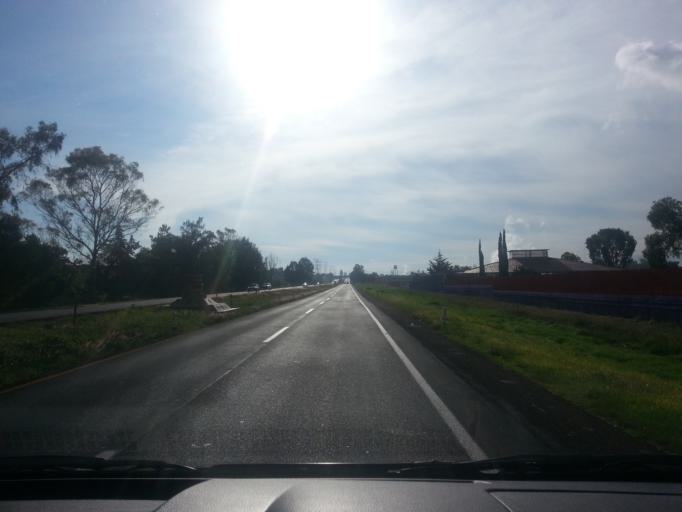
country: MX
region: Mexico
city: Santo Tomas Chiconautla
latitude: 19.6227
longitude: -98.9960
